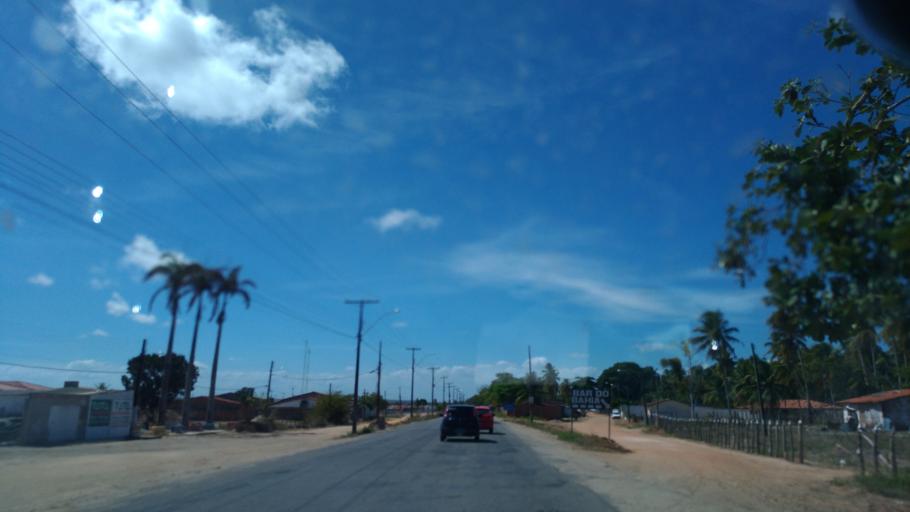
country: BR
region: Alagoas
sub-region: Marechal Deodoro
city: Marechal Deodoro
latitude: -9.7540
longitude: -35.8723
